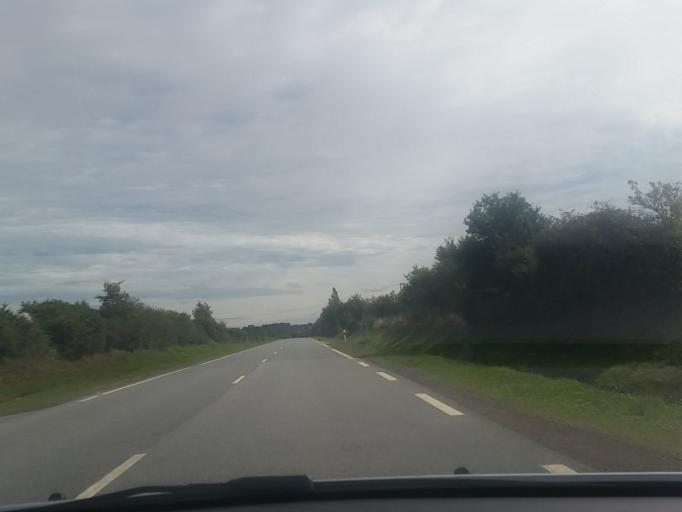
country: FR
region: Brittany
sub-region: Departement d'Ille-et-Vilaine
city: Martigne-Ferchaud
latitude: 47.8429
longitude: -1.3137
